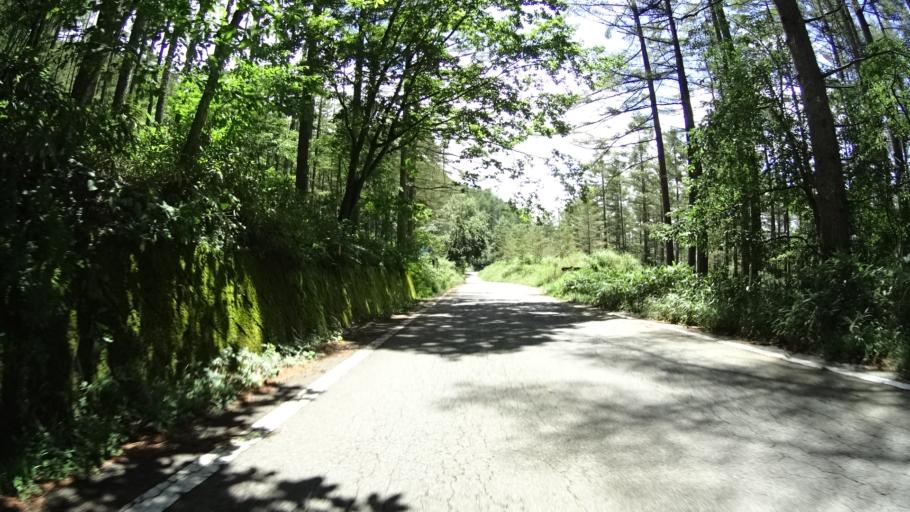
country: JP
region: Yamanashi
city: Enzan
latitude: 35.7301
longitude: 138.8433
